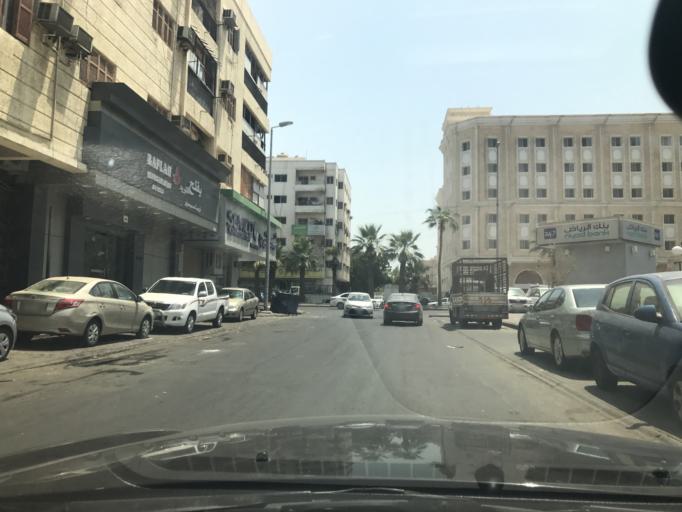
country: SA
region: Makkah
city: Jeddah
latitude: 21.4693
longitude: 39.1854
